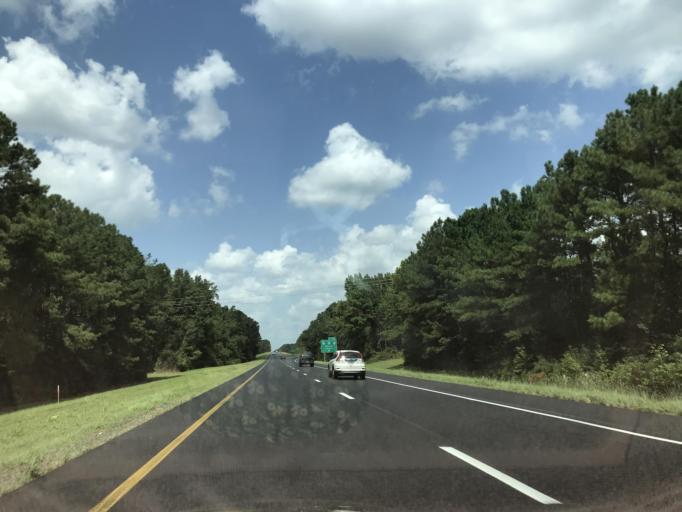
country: US
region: North Carolina
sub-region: Duplin County
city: Warsaw
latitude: 34.9866
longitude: -78.1310
